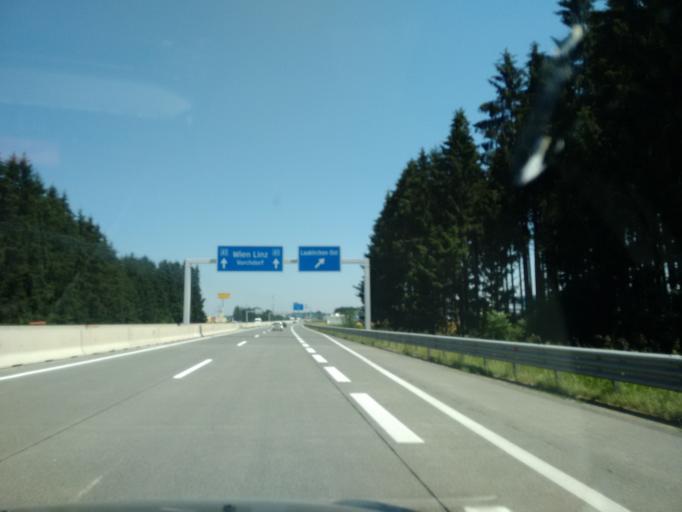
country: AT
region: Upper Austria
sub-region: Politischer Bezirk Gmunden
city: Laakirchen
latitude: 48.0048
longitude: 13.8414
